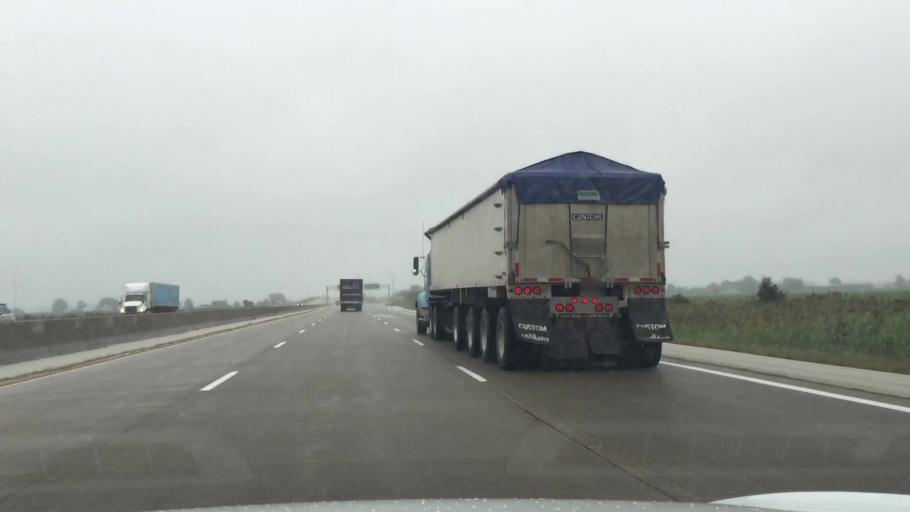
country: US
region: Michigan
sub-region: Wayne County
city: Grosse Pointe Farms
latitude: 42.2335
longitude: -82.6484
